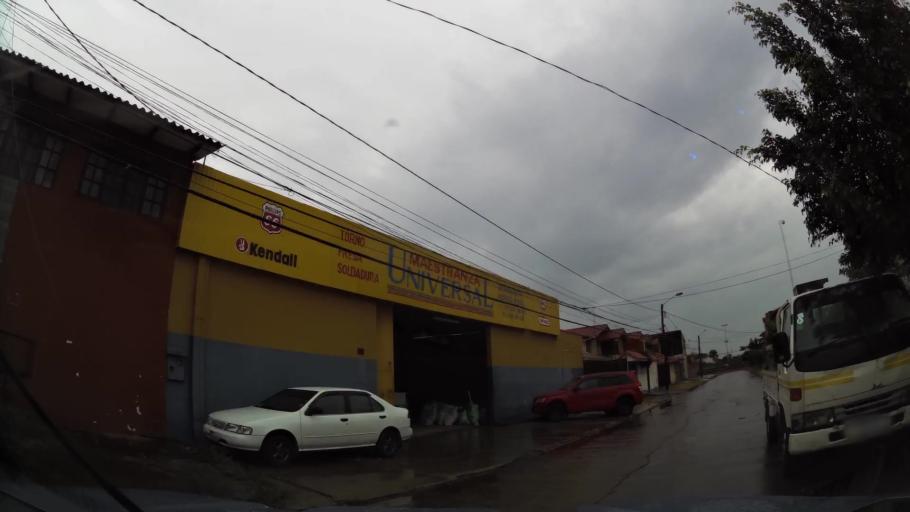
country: BO
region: Santa Cruz
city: Santa Cruz de la Sierra
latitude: -17.7796
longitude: -63.1500
